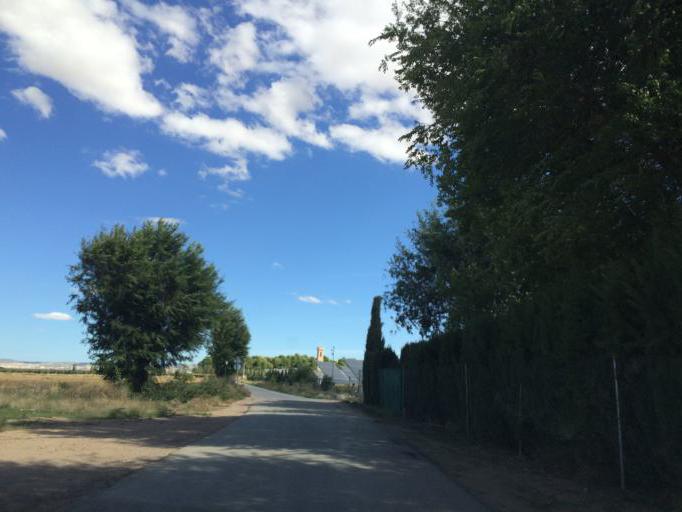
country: ES
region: Castille-La Mancha
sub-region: Provincia de Albacete
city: Albacete
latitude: 38.9298
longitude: -1.8680
